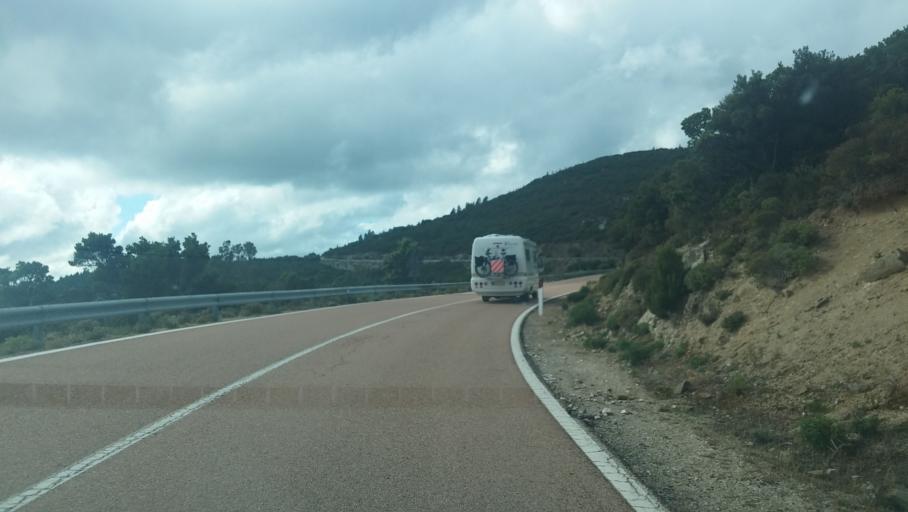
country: IT
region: Sardinia
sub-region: Provincia di Ogliastra
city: Urzulei
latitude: 40.1719
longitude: 9.5271
